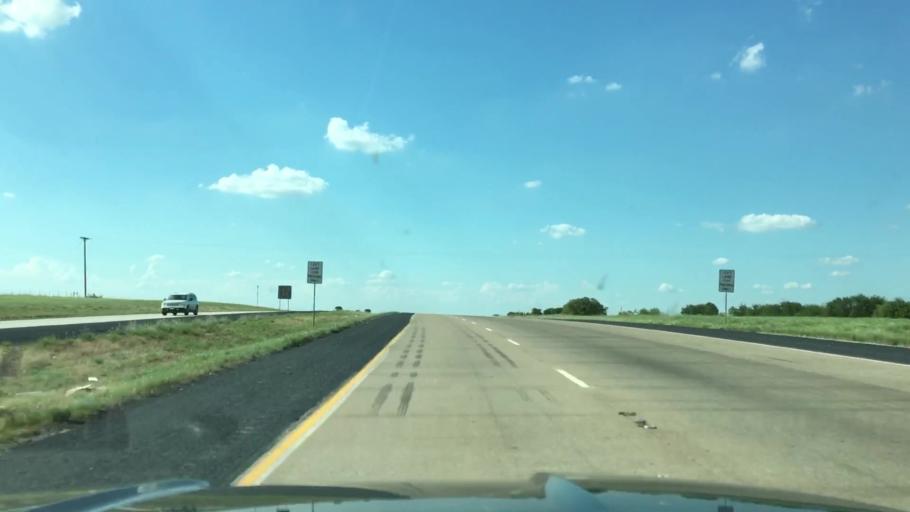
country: US
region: Texas
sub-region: Wise County
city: New Fairview
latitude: 33.1065
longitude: -97.4740
